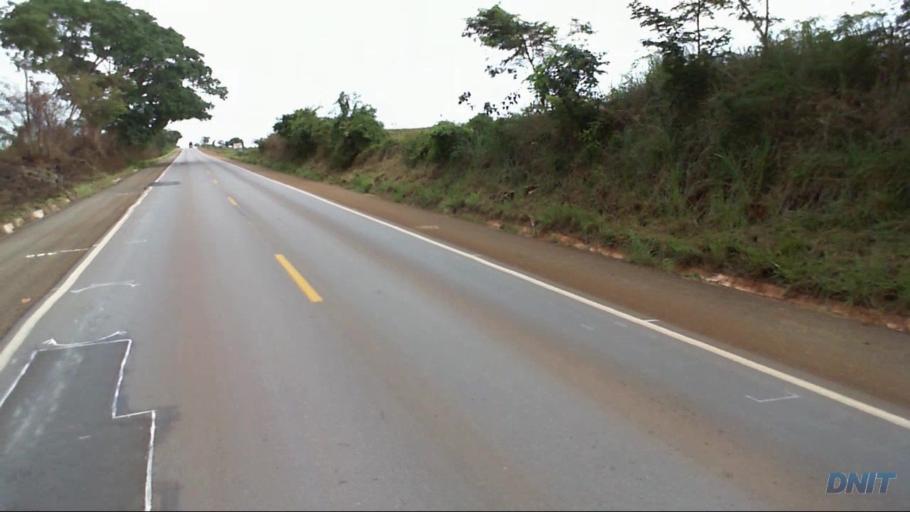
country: BR
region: Goias
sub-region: Uruacu
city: Uruacu
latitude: -14.6826
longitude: -49.1345
